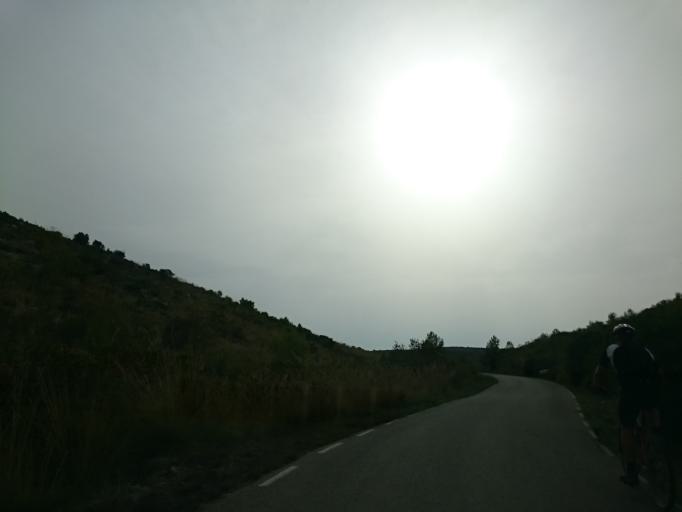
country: ES
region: Catalonia
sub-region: Provincia de Barcelona
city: Olivella
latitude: 41.3046
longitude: 1.8272
